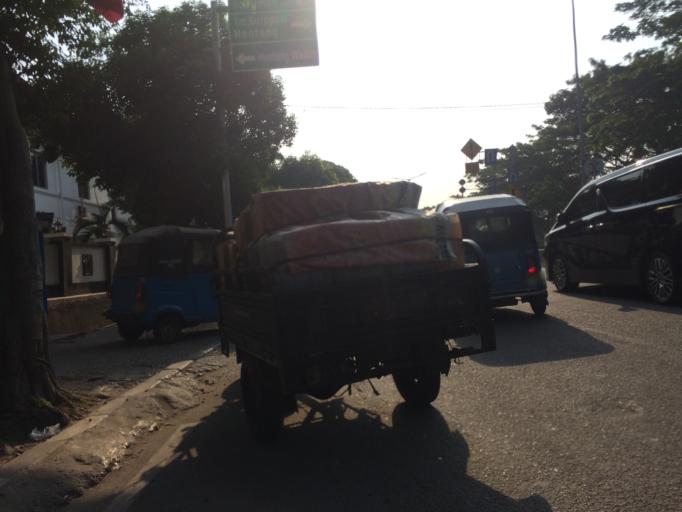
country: ID
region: Jakarta Raya
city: Jakarta
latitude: -6.2070
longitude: 106.8402
